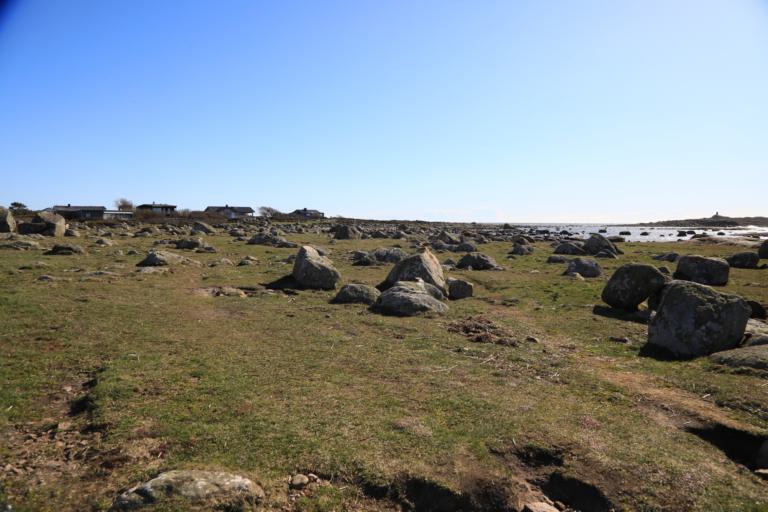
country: SE
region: Halland
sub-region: Varbergs Kommun
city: Traslovslage
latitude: 57.0684
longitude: 12.2530
